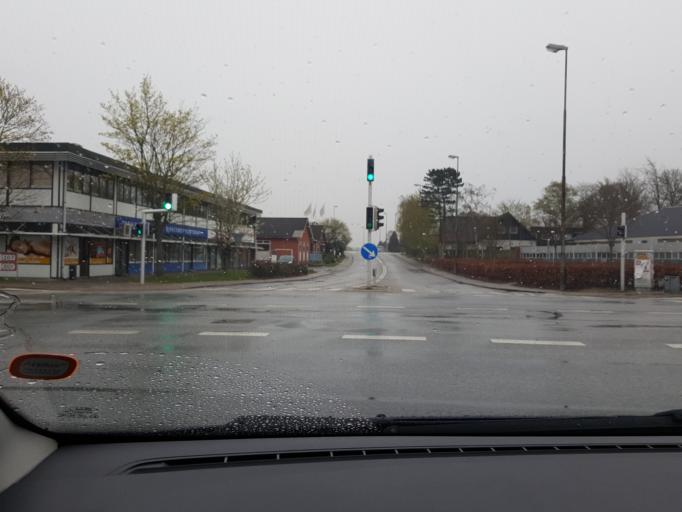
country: DK
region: Capital Region
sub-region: Rudersdal Kommune
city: Birkerod
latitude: 55.8410
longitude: 12.4364
